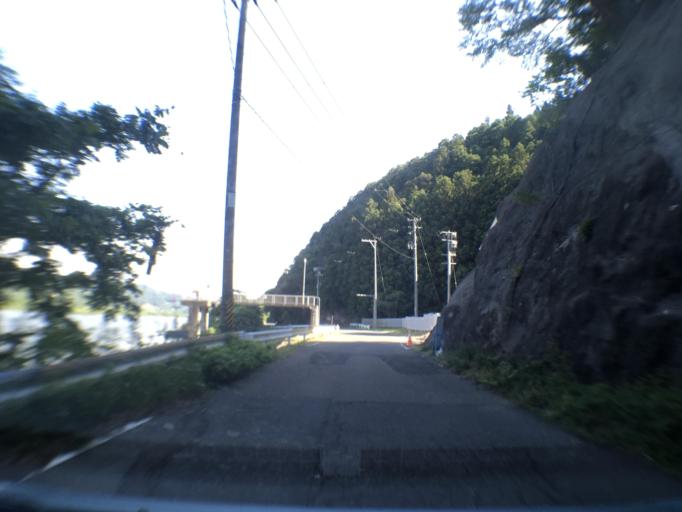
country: JP
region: Miyagi
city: Wakuya
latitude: 38.6280
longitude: 141.2892
